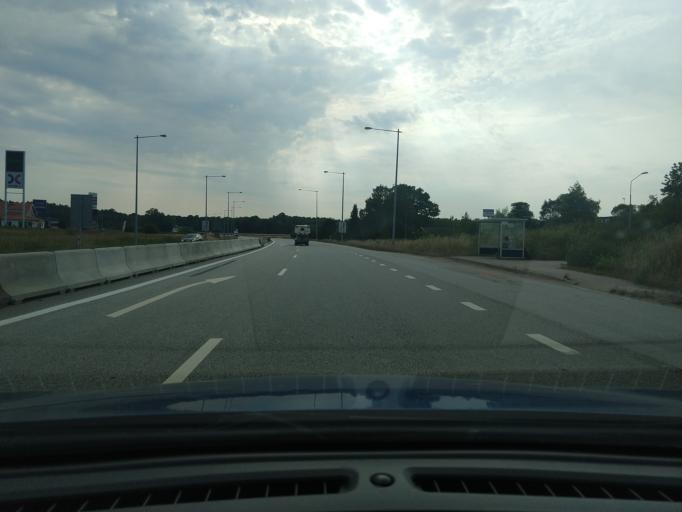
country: SE
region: Blekinge
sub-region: Karlskrona Kommun
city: Nattraby
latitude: 56.2075
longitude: 15.5281
